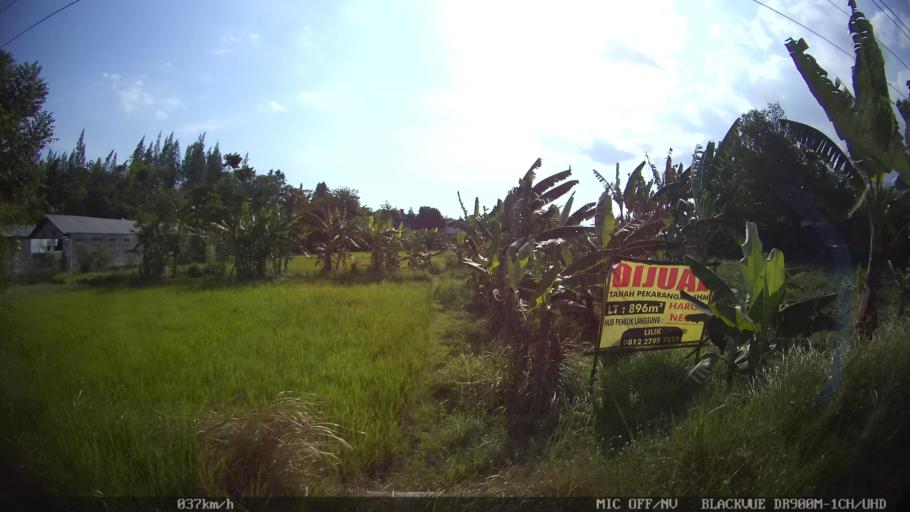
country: ID
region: Daerah Istimewa Yogyakarta
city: Kasihan
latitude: -7.8336
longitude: 110.3447
